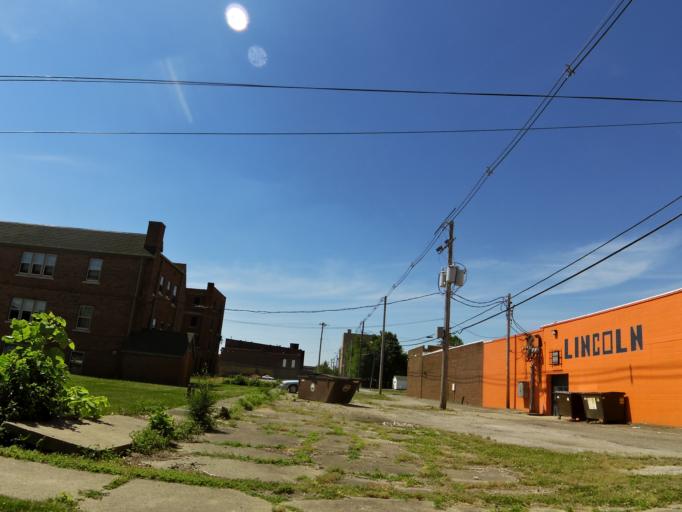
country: US
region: Illinois
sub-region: Vermilion County
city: Danville
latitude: 40.1291
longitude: -87.6321
